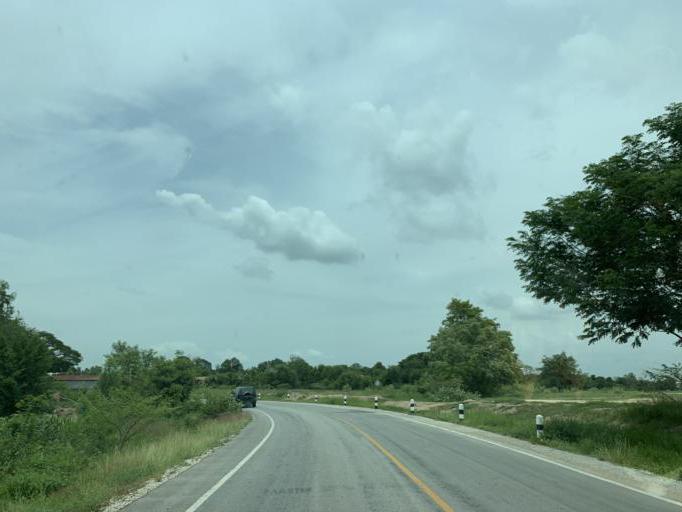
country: TH
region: Uthai Thani
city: Uthai Thani
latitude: 15.4039
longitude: 100.0261
